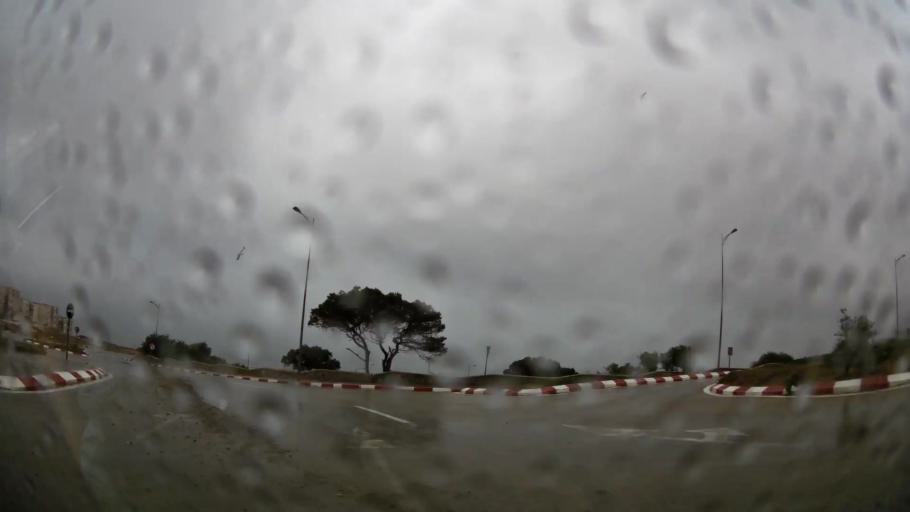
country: MA
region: Taza-Al Hoceima-Taounate
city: Al Hoceima
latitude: 35.2501
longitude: -3.9449
